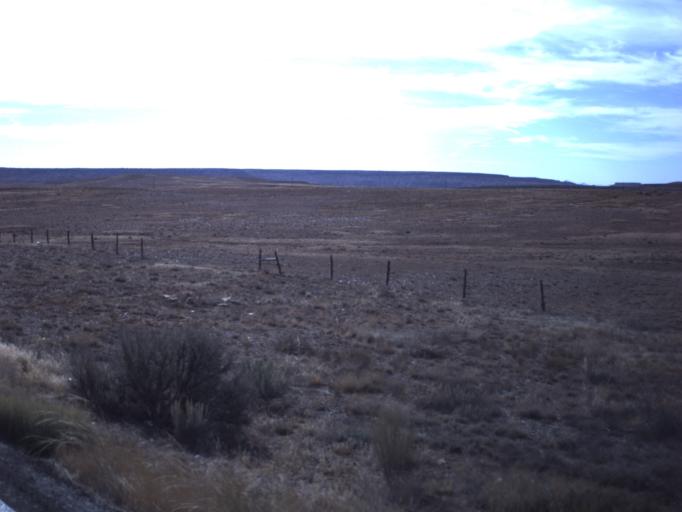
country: US
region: Utah
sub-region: San Juan County
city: Blanding
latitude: 37.4211
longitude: -109.4616
